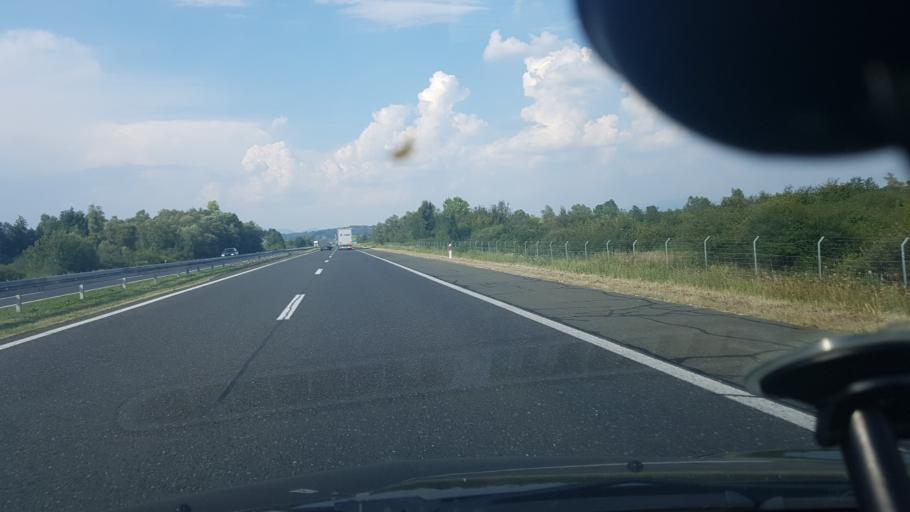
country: HR
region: Zagrebacka
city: Jakovlje
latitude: 45.9844
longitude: 15.8578
